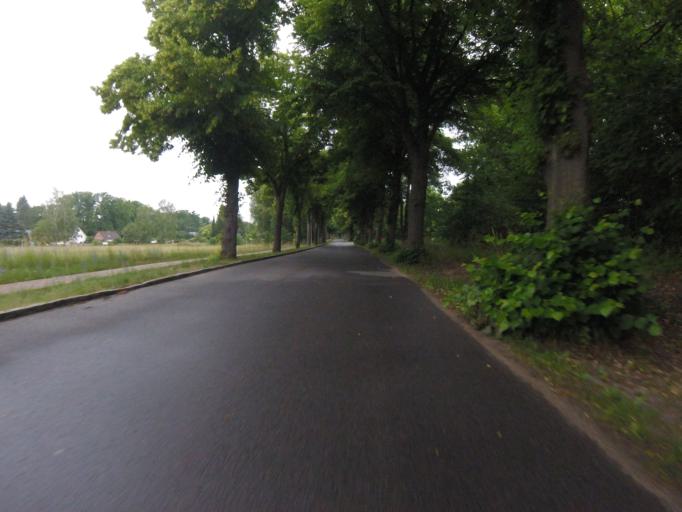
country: DE
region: Brandenburg
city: Konigs Wusterhausen
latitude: 52.2746
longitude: 13.6004
